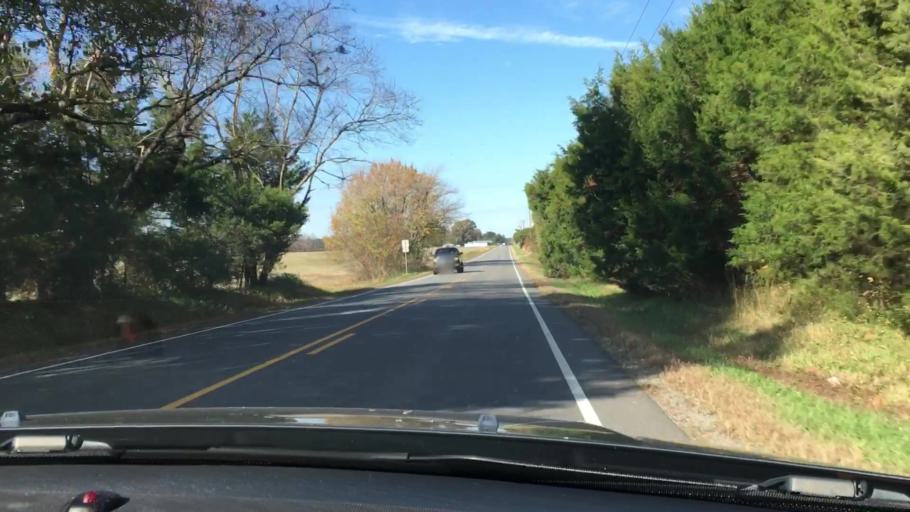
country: US
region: Virginia
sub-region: King and Queen County
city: King and Queen Court House
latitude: 37.6262
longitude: -76.9310
